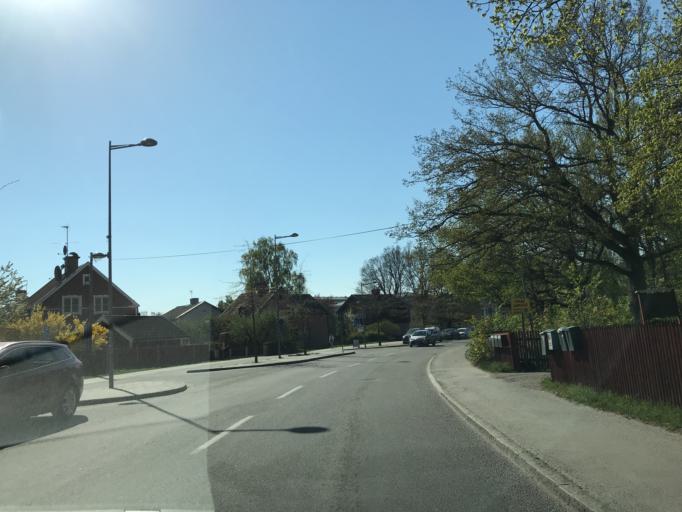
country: SE
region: Stockholm
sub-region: Stockholms Kommun
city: Arsta
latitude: 59.2791
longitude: 18.0084
